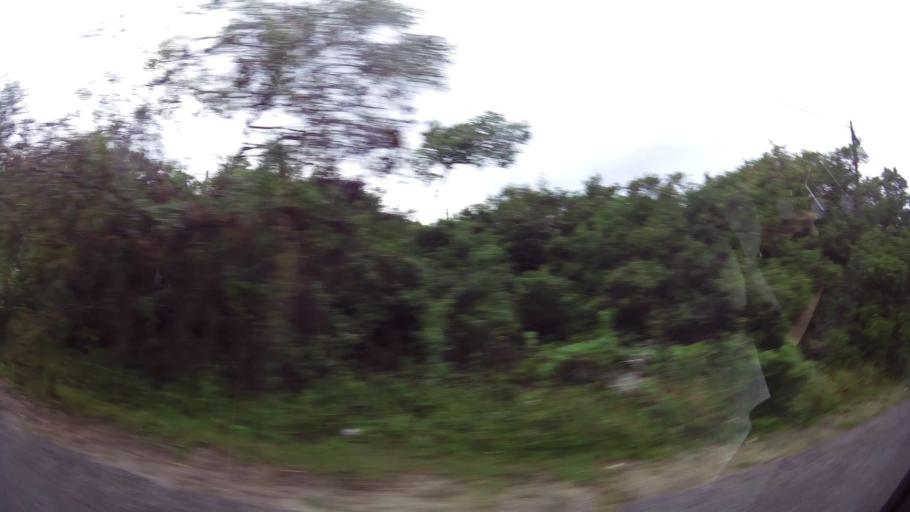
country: ZA
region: Eastern Cape
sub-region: Nelson Mandela Bay Metropolitan Municipality
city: Port Elizabeth
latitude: -34.0186
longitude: 25.5103
